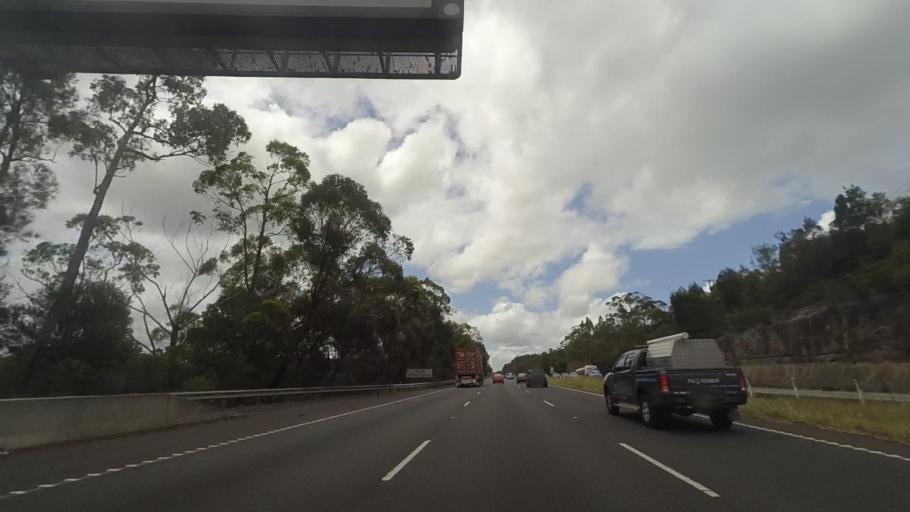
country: AU
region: New South Wales
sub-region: Gosford Shire
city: Point Clare
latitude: -33.4372
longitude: 151.2199
